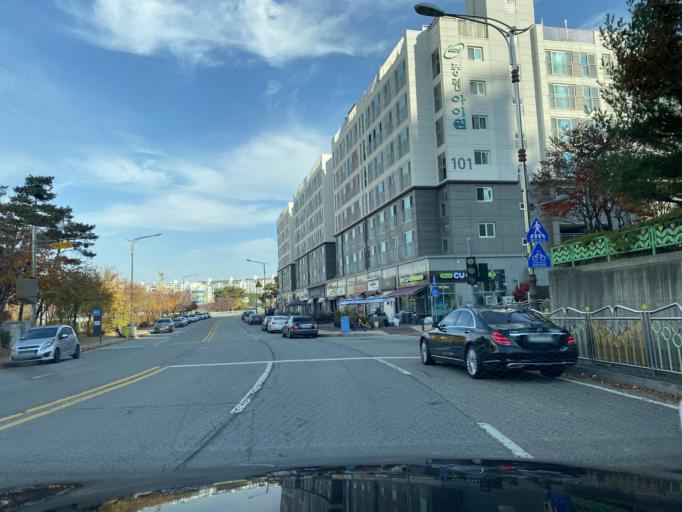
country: KR
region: Chungcheongnam-do
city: Cheonan
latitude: 36.8002
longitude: 127.1085
